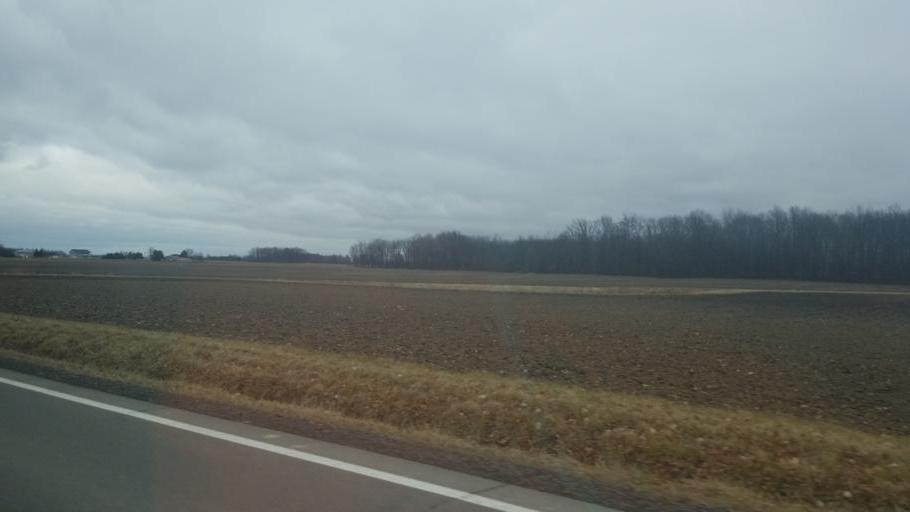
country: US
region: Ohio
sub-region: Crawford County
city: Crestline
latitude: 40.8192
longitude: -82.7303
